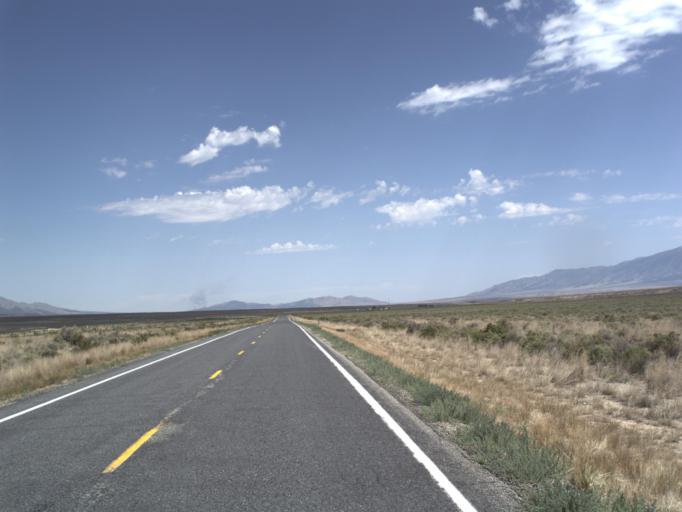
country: US
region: Utah
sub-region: Tooele County
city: Tooele
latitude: 40.1344
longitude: -112.4308
